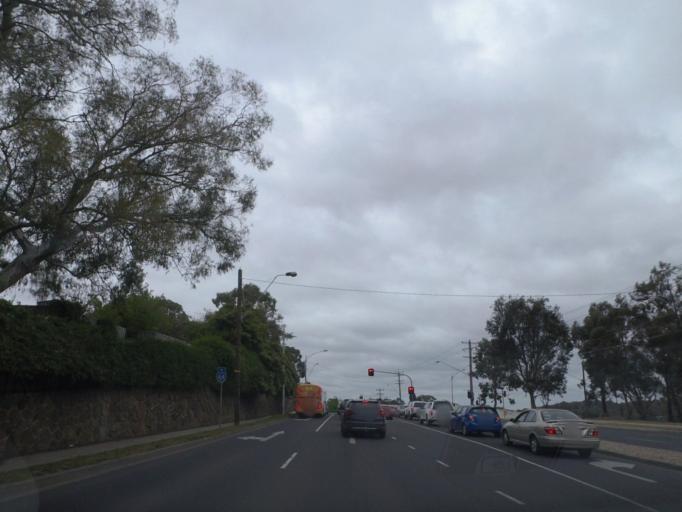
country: AU
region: Victoria
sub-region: Nillumbik
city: Eltham
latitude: -37.7183
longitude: 145.1464
